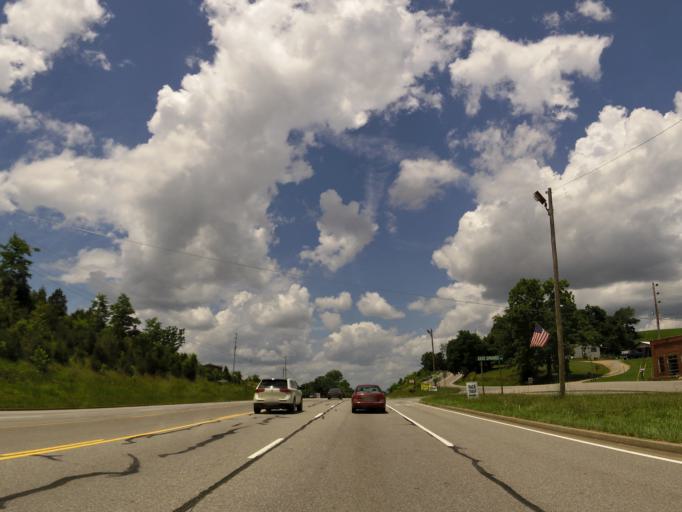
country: US
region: Tennessee
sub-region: Claiborne County
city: Tazewell
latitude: 36.4778
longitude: -83.5827
